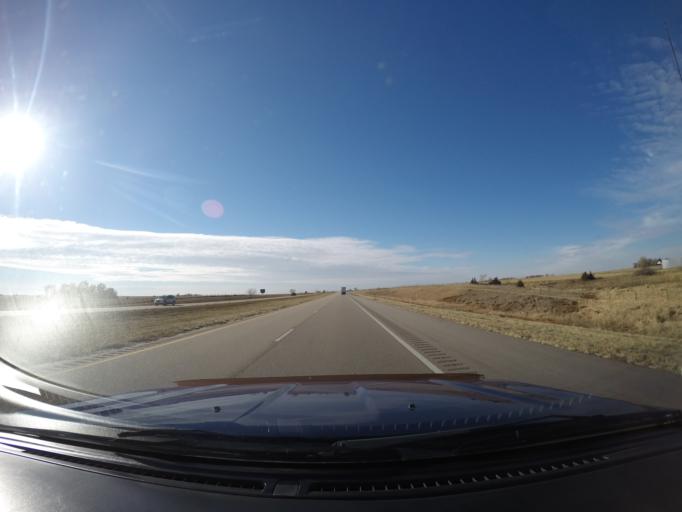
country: US
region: Nebraska
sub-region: Hamilton County
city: Aurora
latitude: 40.8222
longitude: -98.0896
